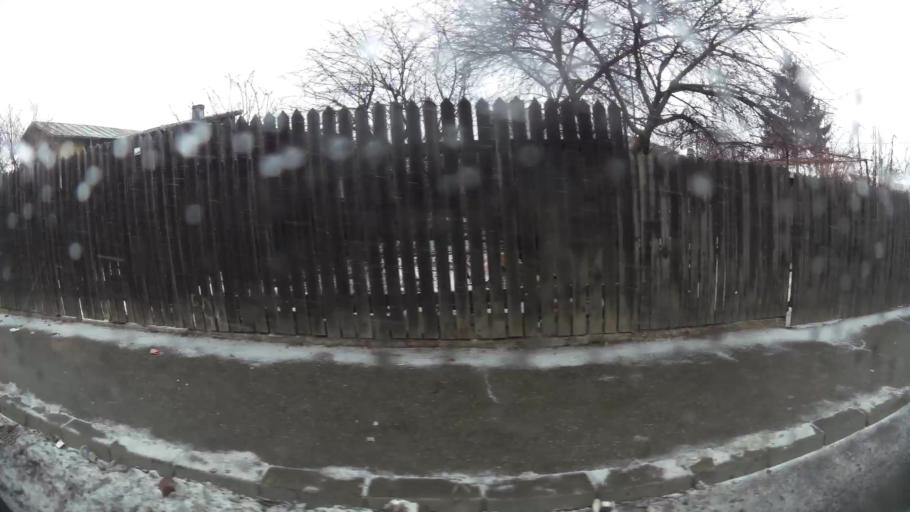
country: RO
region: Prahova
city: Ploiesti
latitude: 44.9558
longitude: 26.0405
